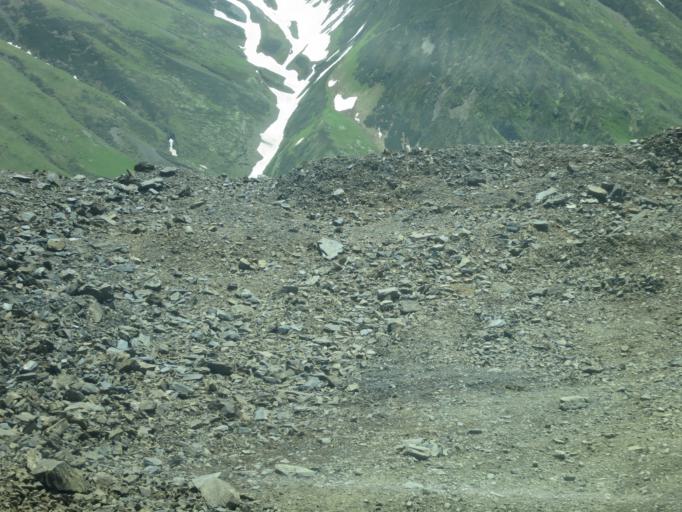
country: GE
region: Kakheti
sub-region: Telavi
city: Telavi
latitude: 42.2721
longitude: 45.4960
